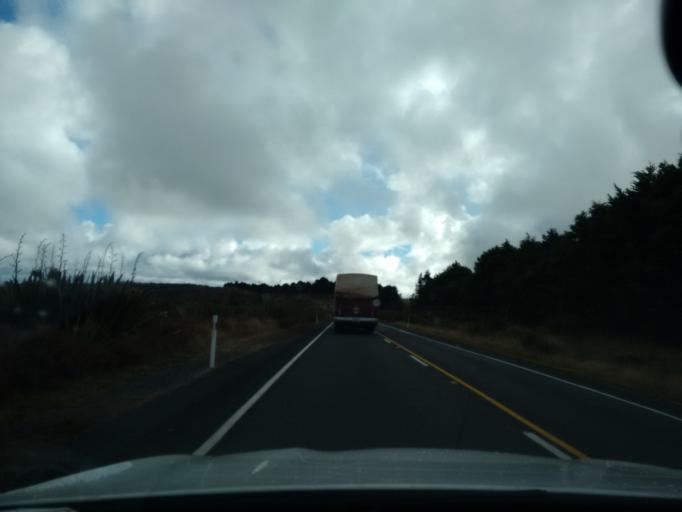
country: NZ
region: Manawatu-Wanganui
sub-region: Ruapehu District
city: Waiouru
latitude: -39.1798
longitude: 175.4519
